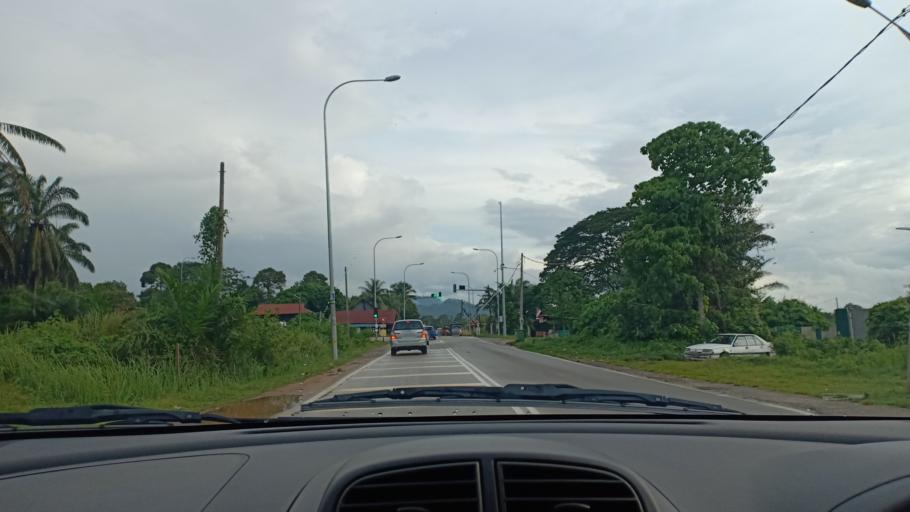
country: MY
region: Penang
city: Tasek Glugor
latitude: 5.4390
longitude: 100.5132
